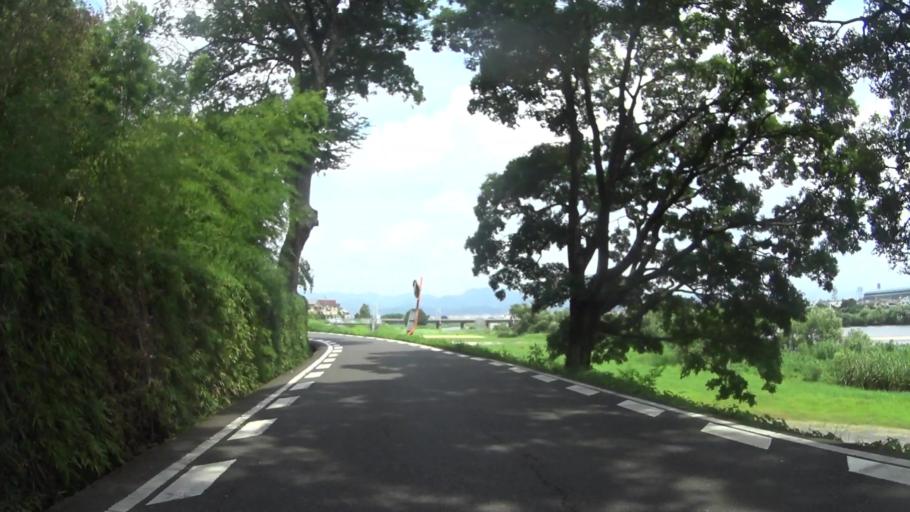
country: JP
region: Kyoto
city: Muko
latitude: 34.9843
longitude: 135.7114
